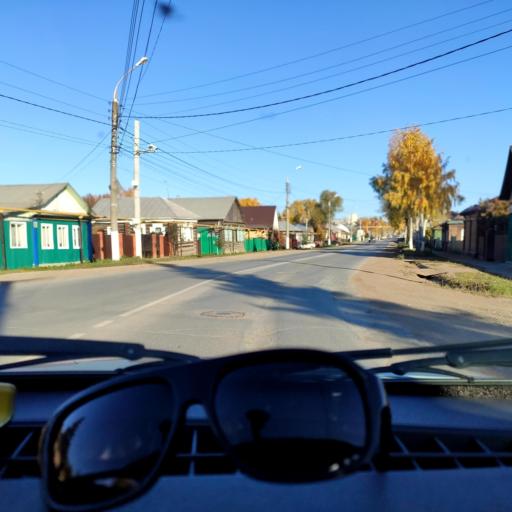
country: RU
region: Bashkortostan
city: Blagoveshchensk
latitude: 55.0342
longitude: 55.9656
